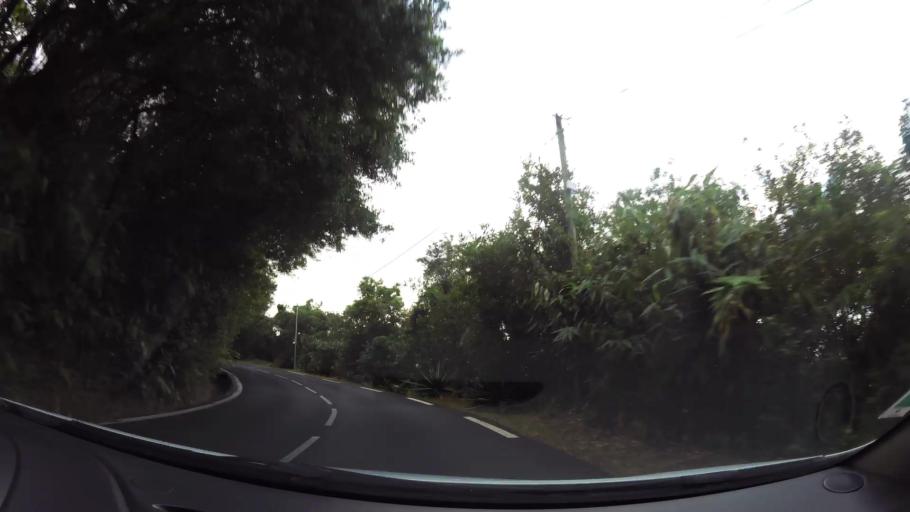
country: RE
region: Reunion
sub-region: Reunion
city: Saint-Denis
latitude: -20.9100
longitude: 55.4419
